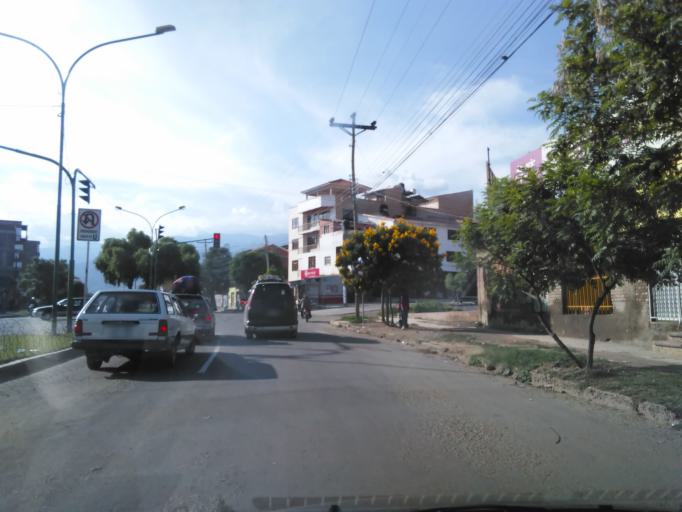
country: BO
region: Cochabamba
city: Cochabamba
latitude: -17.3570
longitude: -66.1845
